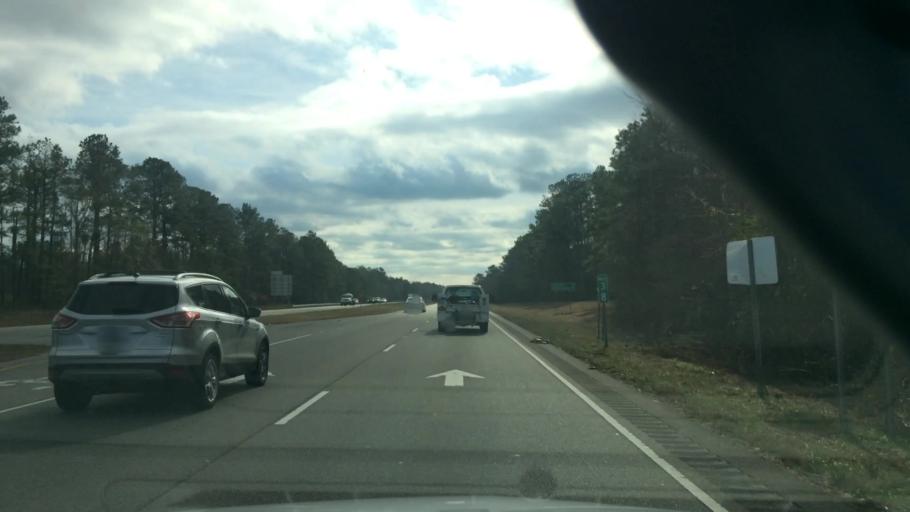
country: US
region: North Carolina
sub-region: Brunswick County
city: Leland
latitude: 34.1704
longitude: -78.0883
